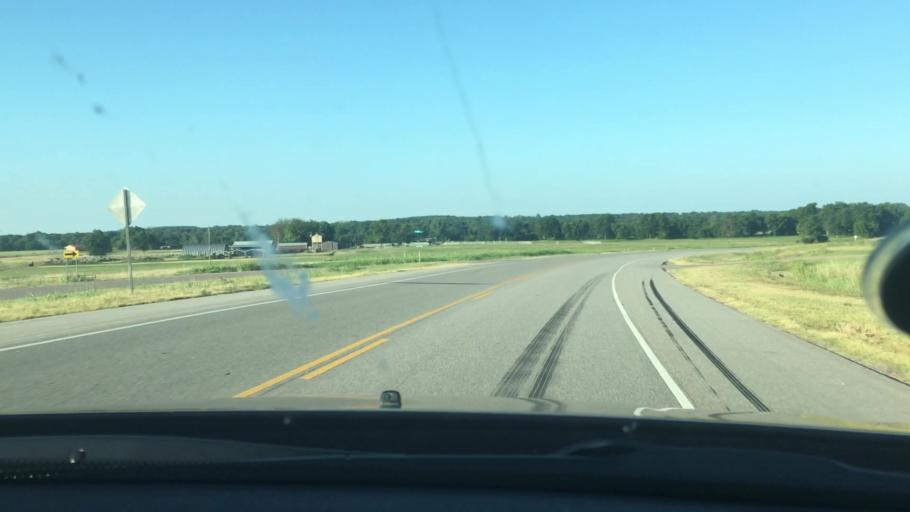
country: US
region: Oklahoma
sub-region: Pontotoc County
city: Ada
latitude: 34.6506
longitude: -96.7961
